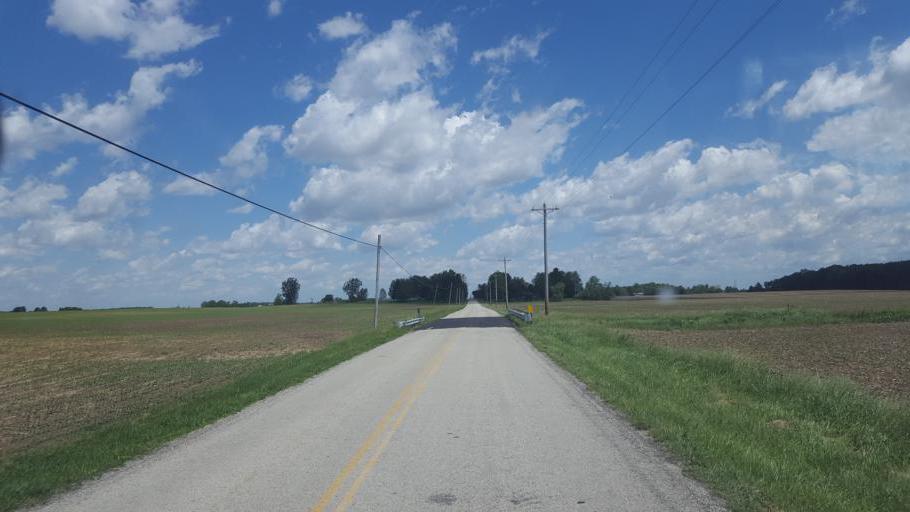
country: US
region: Ohio
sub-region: Richland County
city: Shelby
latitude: 40.8601
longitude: -82.7198
